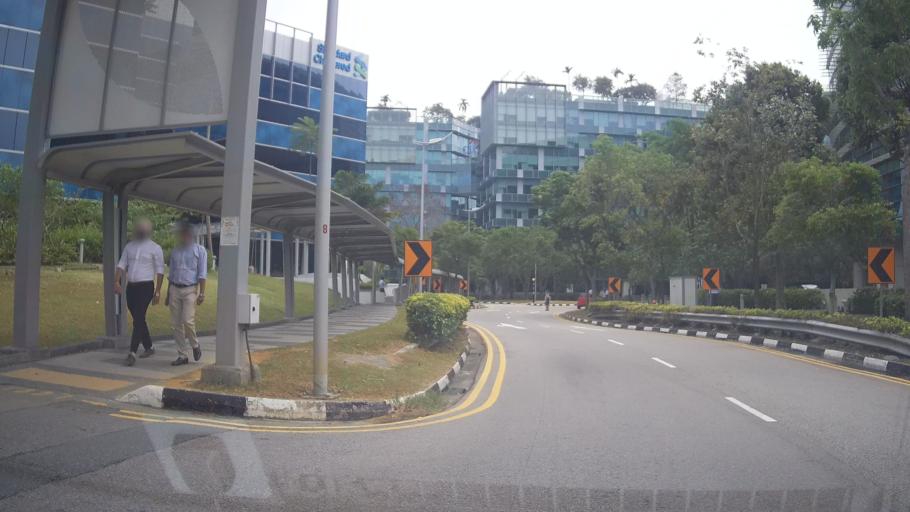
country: SG
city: Singapore
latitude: 1.3349
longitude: 103.9670
